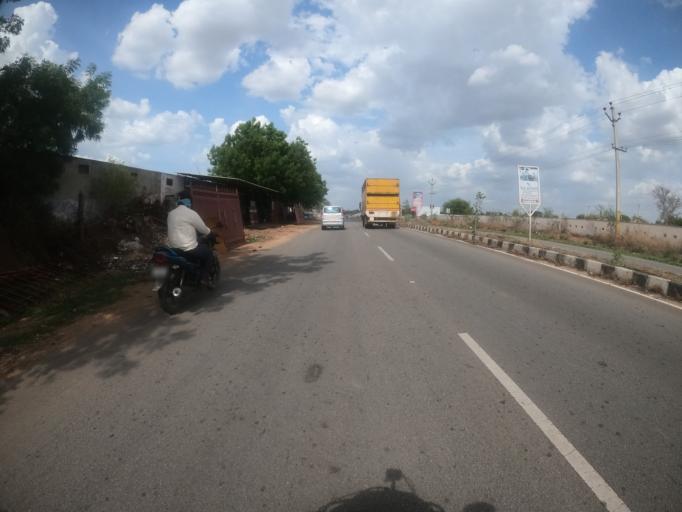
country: IN
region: Telangana
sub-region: Rangareddi
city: Sriramnagar
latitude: 17.3313
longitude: 78.2899
